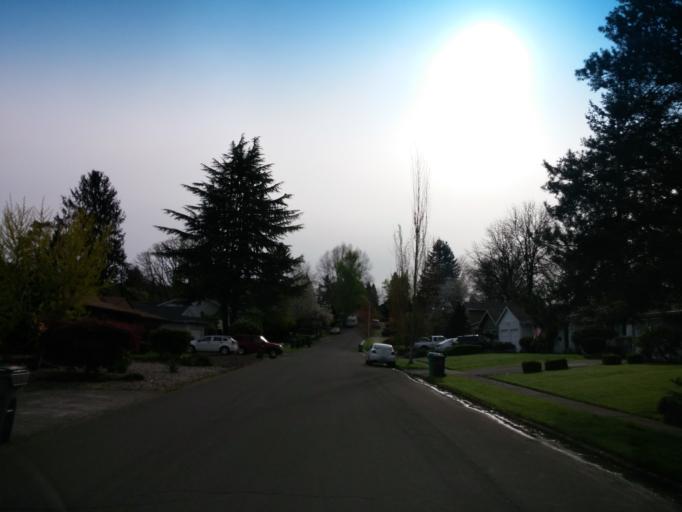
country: US
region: Oregon
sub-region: Washington County
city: Cedar Hills
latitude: 45.5112
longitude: -122.8079
